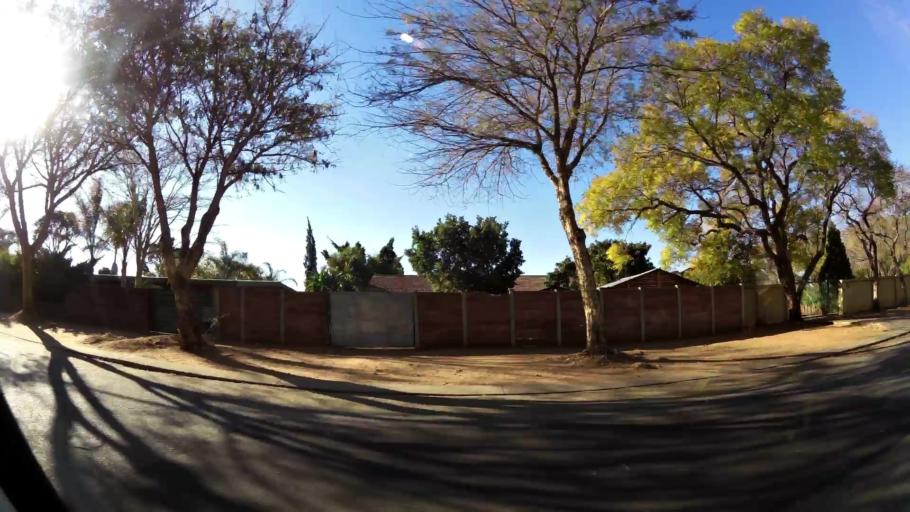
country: ZA
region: Limpopo
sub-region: Capricorn District Municipality
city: Polokwane
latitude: -23.8908
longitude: 29.4852
